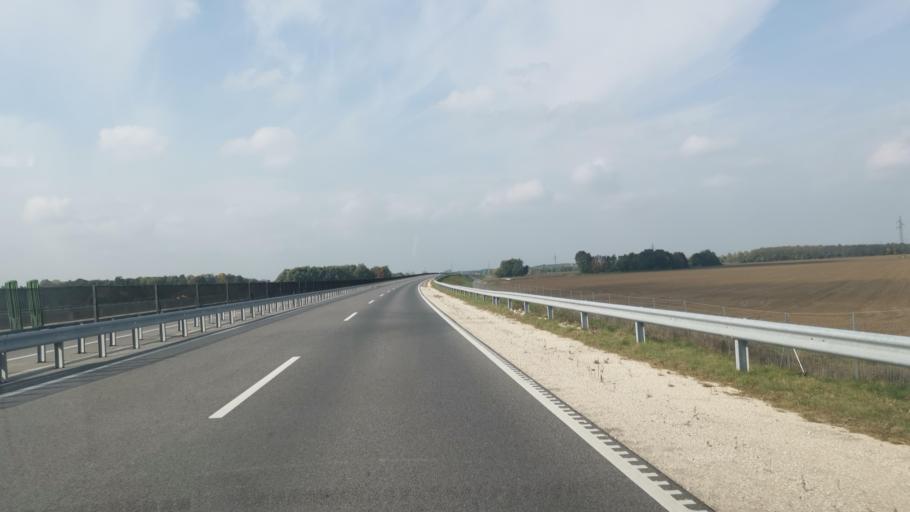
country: HU
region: Gyor-Moson-Sopron
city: Kapuvar
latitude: 47.5724
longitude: 17.0068
